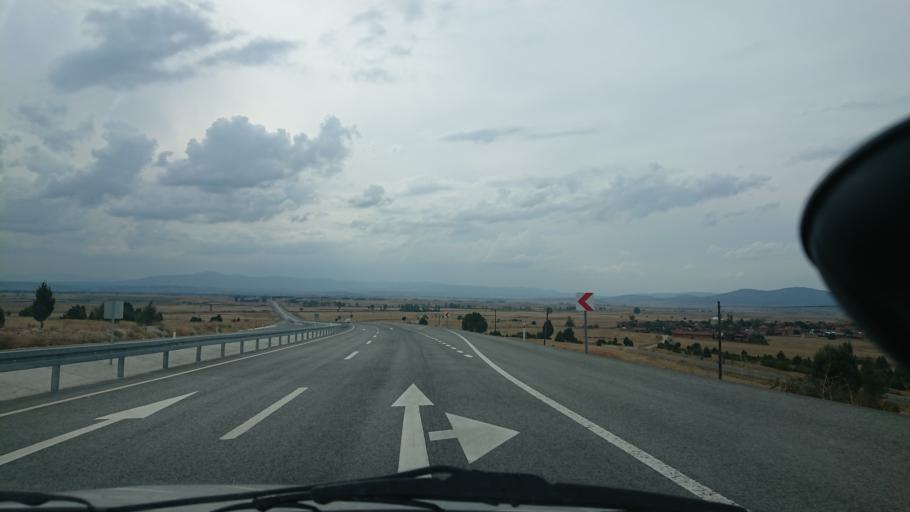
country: TR
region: Kuetahya
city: Cavdarhisar
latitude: 39.2265
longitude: 29.7150
